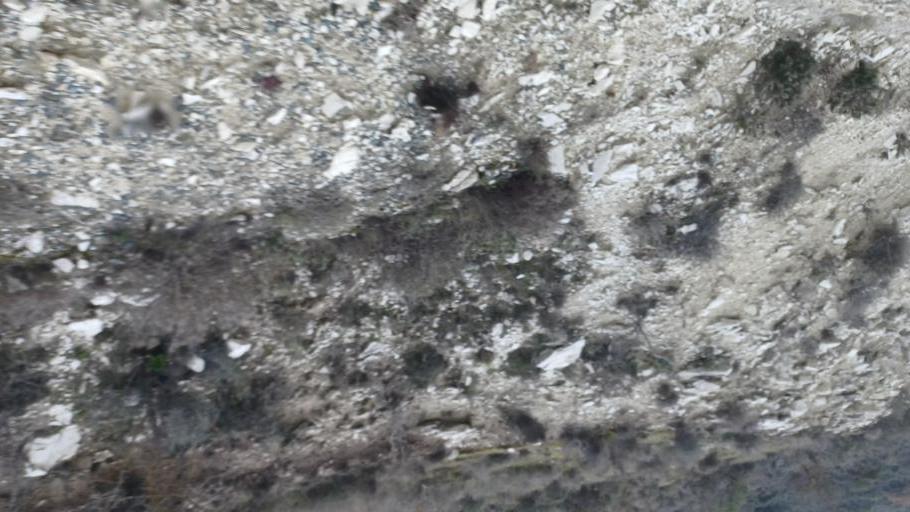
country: CY
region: Limassol
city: Pachna
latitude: 34.8716
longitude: 32.7736
